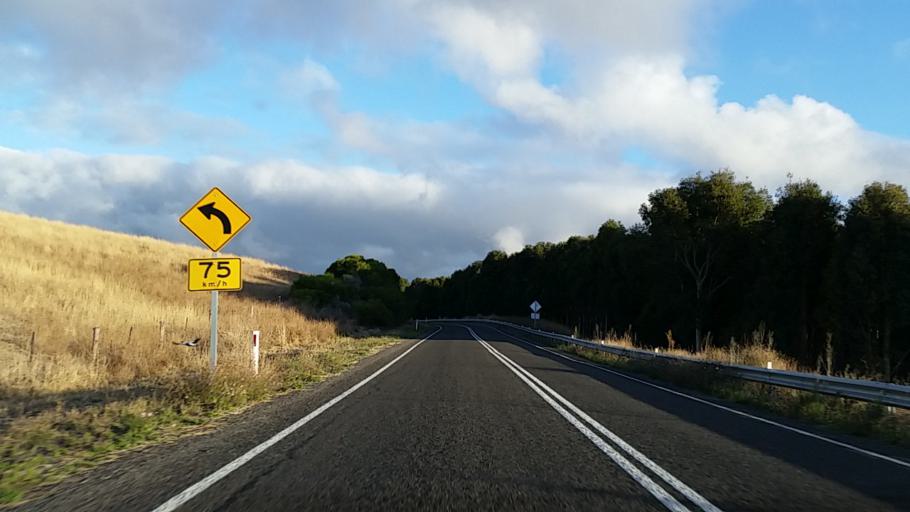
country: AU
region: South Australia
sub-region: Yankalilla
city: Normanville
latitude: -35.5576
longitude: 138.1982
